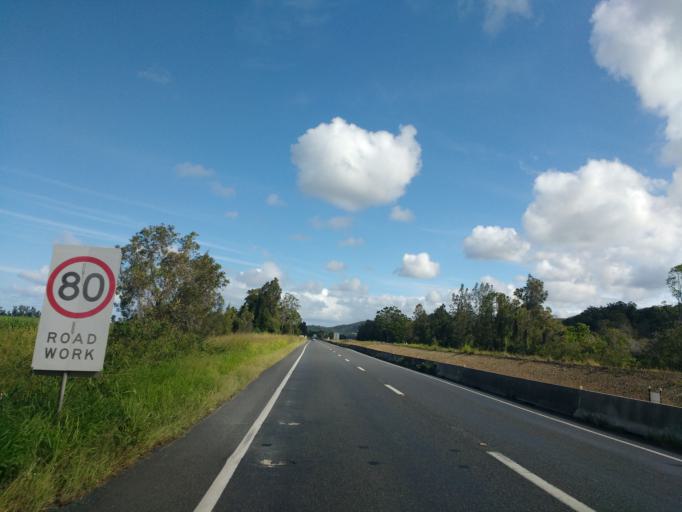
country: AU
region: New South Wales
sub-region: Ballina
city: Ballina
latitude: -28.8729
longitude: 153.4904
